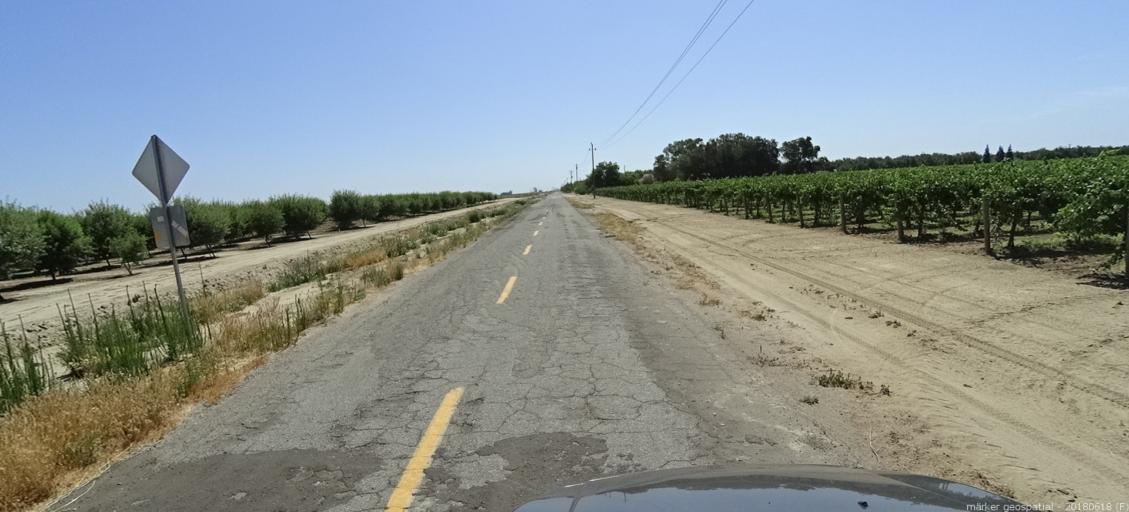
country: US
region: California
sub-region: Madera County
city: Parkwood
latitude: 36.8802
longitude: -120.1808
